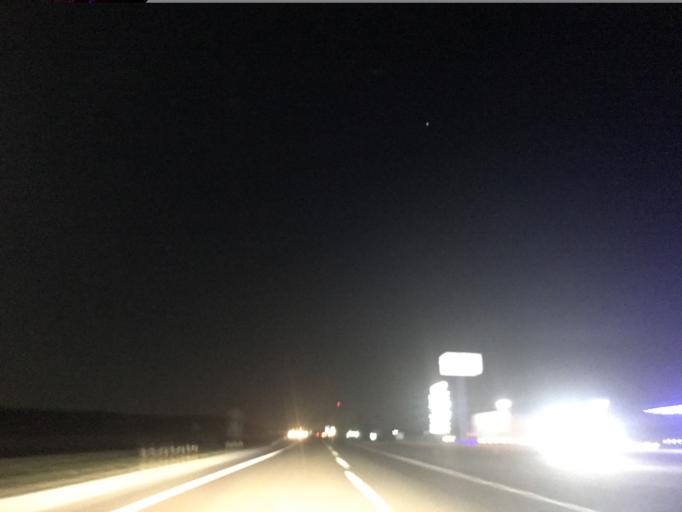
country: TR
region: Nigde
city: Ulukisla
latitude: 37.6578
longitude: 34.3438
